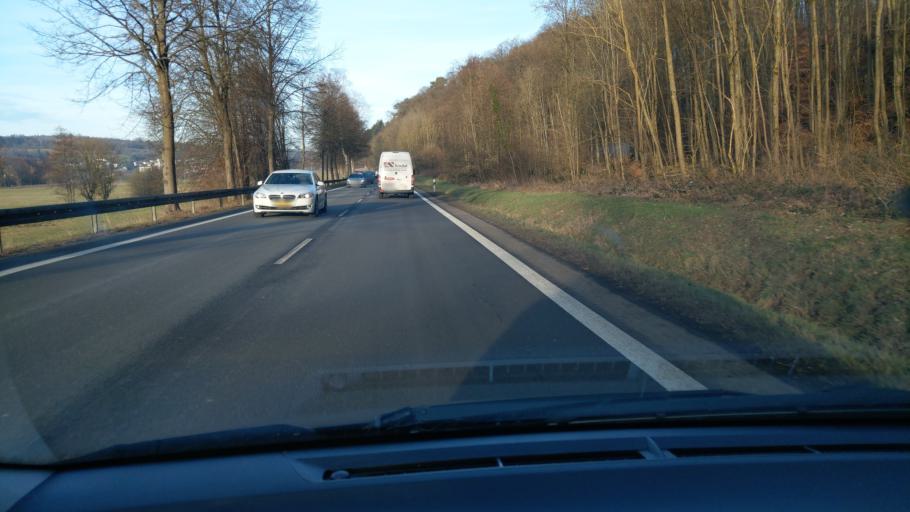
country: DE
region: Saarland
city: Blieskastel
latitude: 49.2498
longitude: 7.2772
